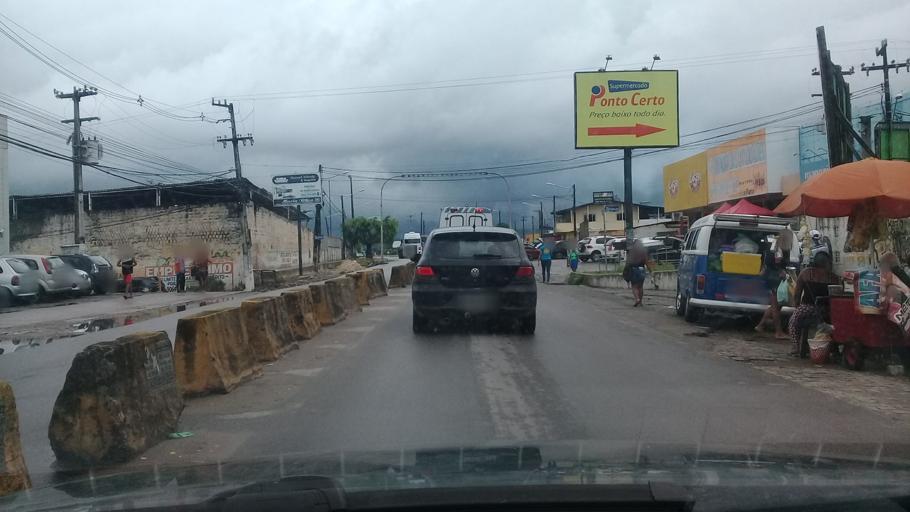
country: BR
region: Pernambuco
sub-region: Igarassu
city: Igarassu
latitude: -7.8298
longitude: -34.9103
